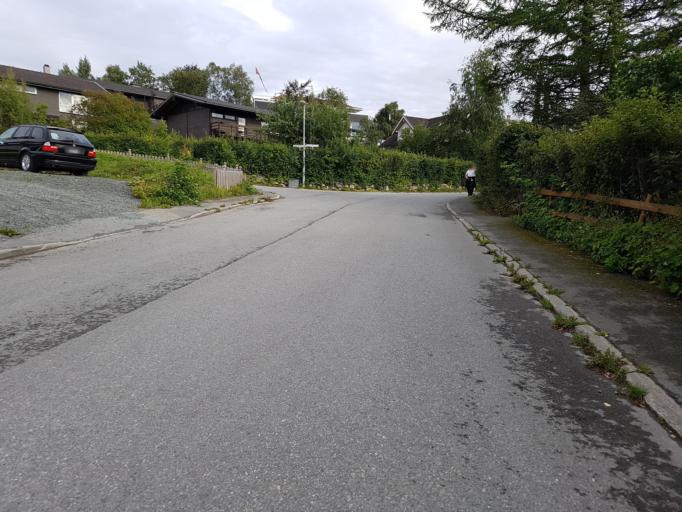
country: NO
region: Sor-Trondelag
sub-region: Trondheim
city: Trondheim
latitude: 63.4034
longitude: 10.4324
